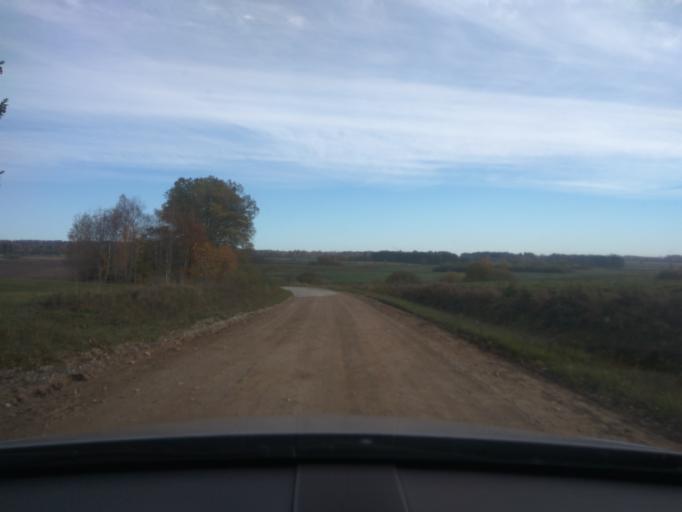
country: LV
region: Alsunga
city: Alsunga
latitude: 56.8684
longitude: 21.6856
